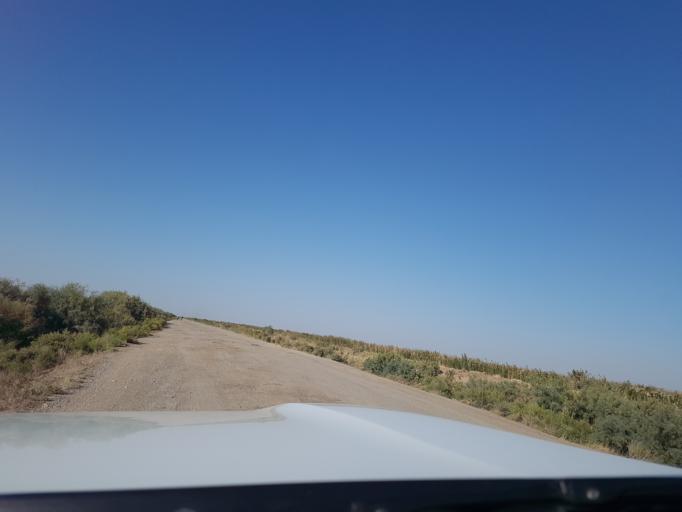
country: IR
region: Razavi Khorasan
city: Sarakhs
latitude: 36.9457
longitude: 61.3788
